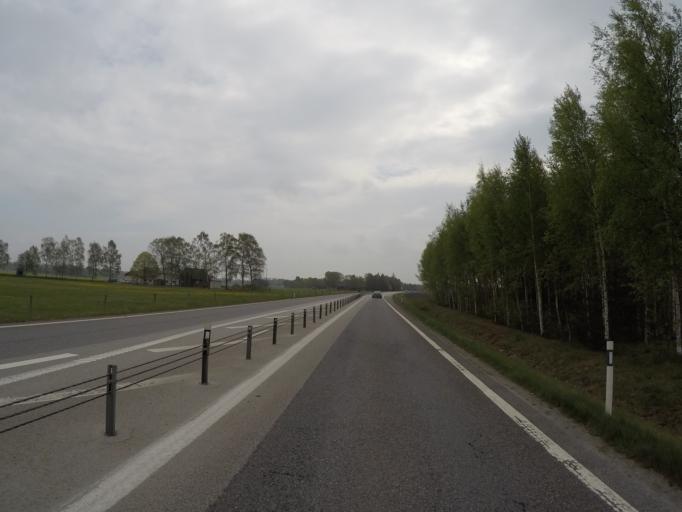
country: SE
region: Halland
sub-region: Laholms Kommun
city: Laholm
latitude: 56.4508
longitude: 13.1167
